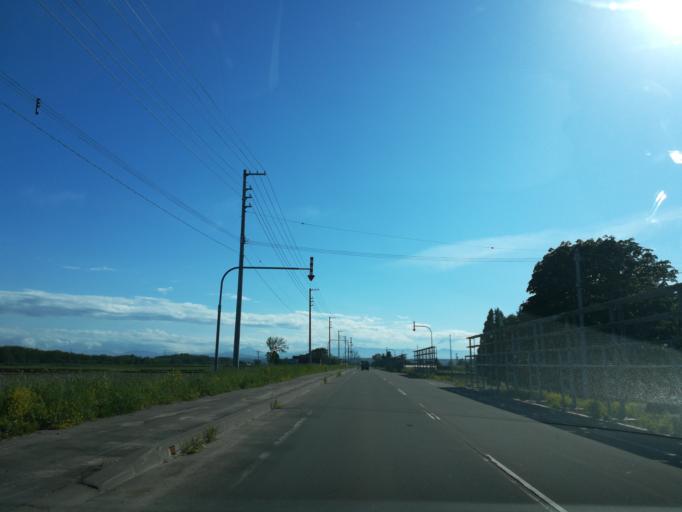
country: JP
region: Hokkaido
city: Ebetsu
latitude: 43.0580
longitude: 141.6183
